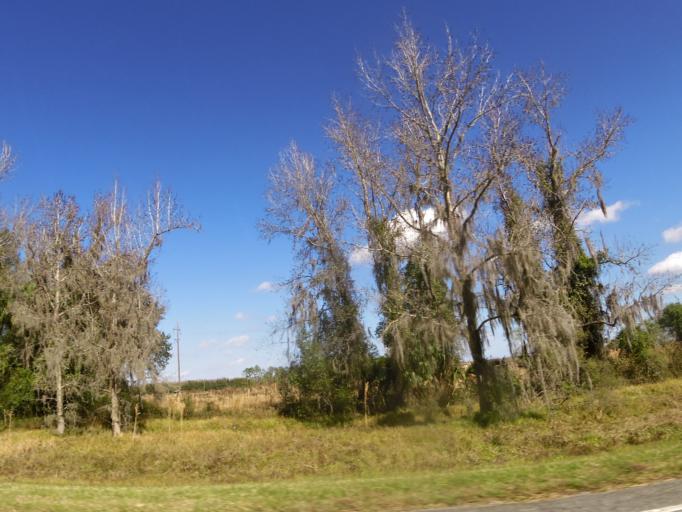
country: US
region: Florida
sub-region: Volusia County
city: De Leon Springs
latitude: 29.1620
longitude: -81.3887
